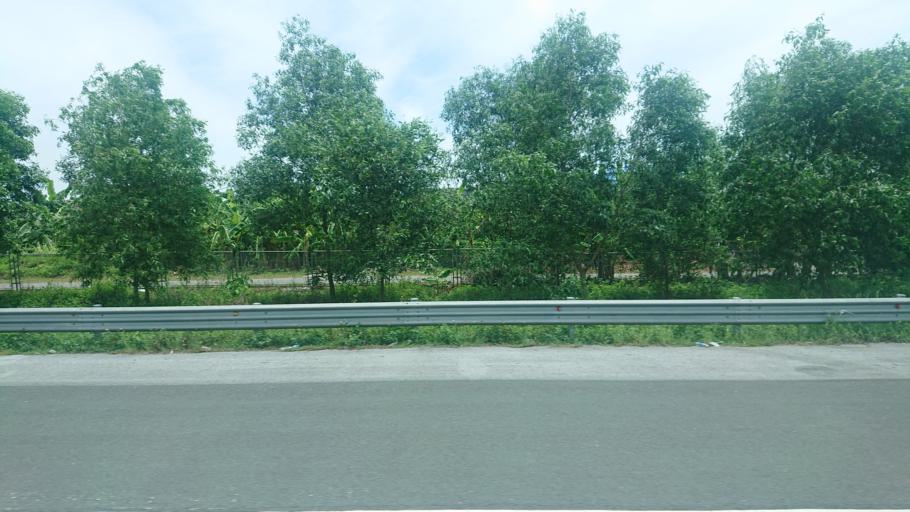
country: VN
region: Hai Phong
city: An Lao
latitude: 20.8161
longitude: 106.4905
